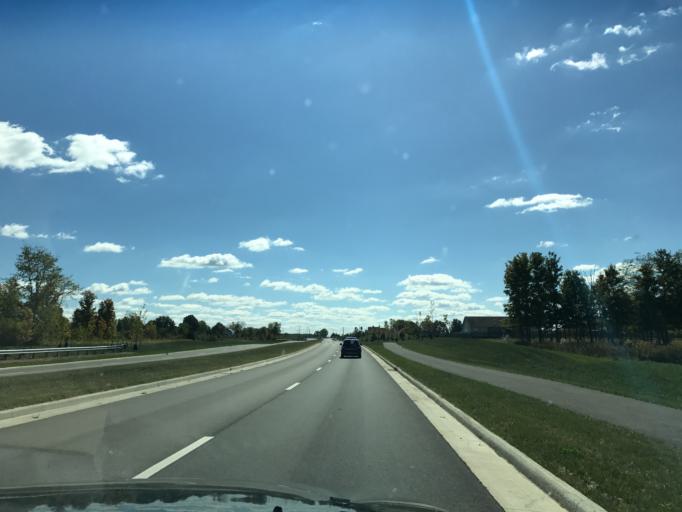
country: US
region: Ohio
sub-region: Delaware County
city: Delaware
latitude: 40.2409
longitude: -83.0948
